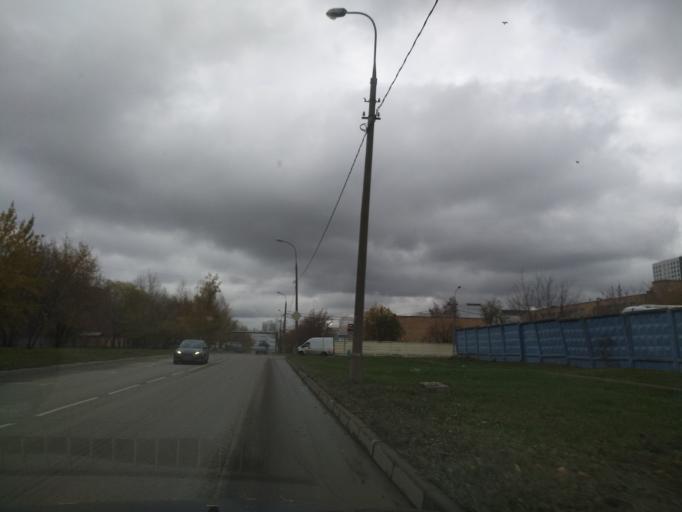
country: RU
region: Moscow
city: Kozeyevo
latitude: 55.8851
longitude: 37.6301
